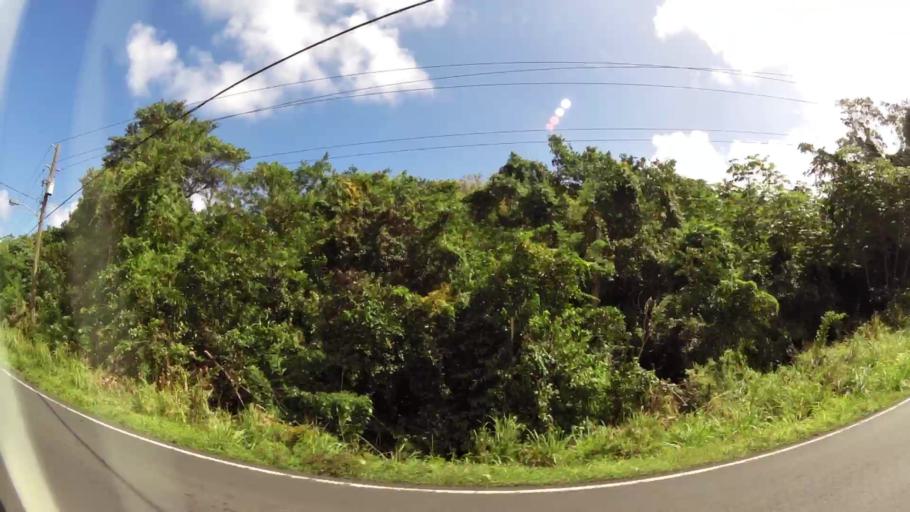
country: LC
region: Micoud Quarter
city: Micoud
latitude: 13.8009
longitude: -60.9050
